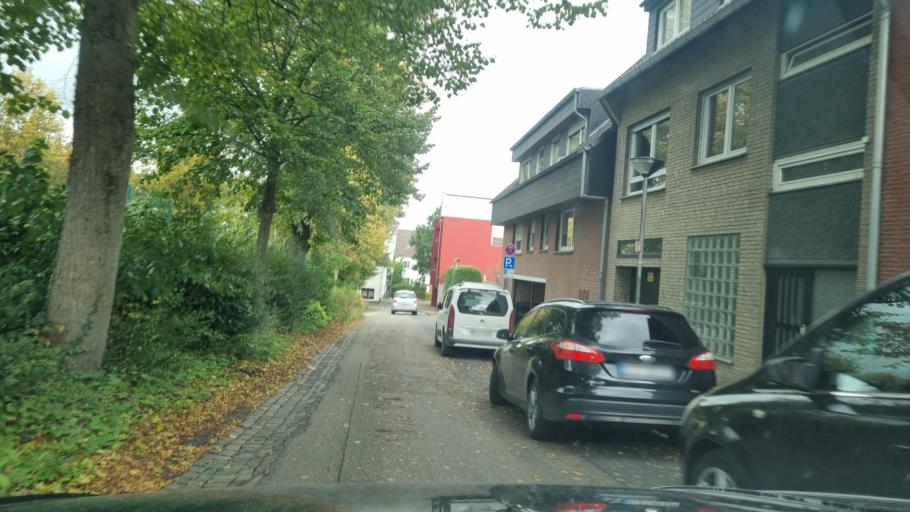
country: DE
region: North Rhine-Westphalia
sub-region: Regierungsbezirk Dusseldorf
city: Kleve
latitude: 51.7886
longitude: 6.1353
